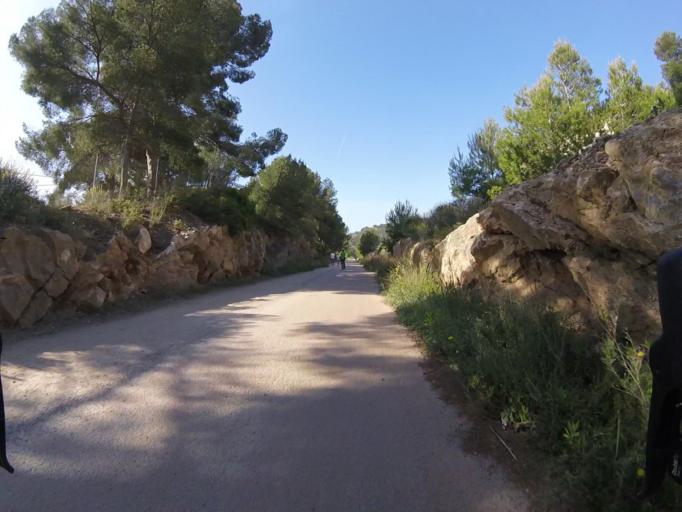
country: ES
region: Valencia
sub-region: Provincia de Castello
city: Orpesa/Oropesa del Mar
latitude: 40.0812
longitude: 0.1358
